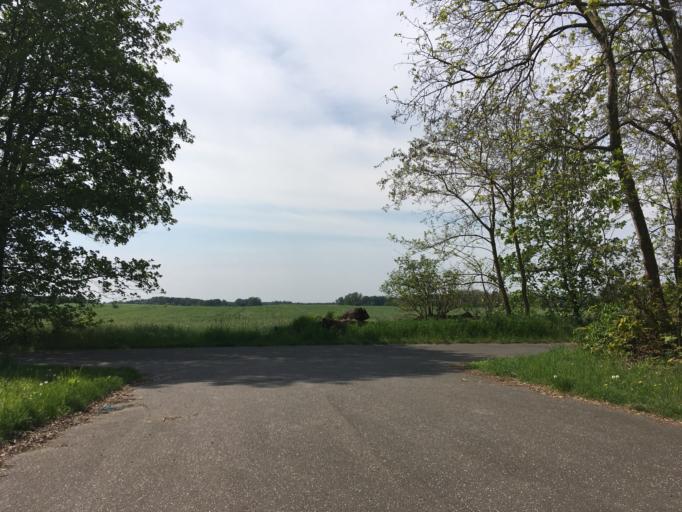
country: DE
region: Brandenburg
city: Werneuchen
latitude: 52.6015
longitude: 13.7309
